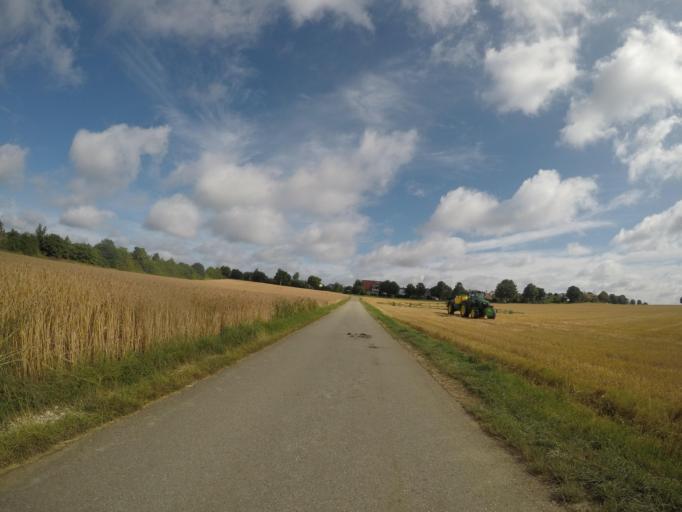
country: DE
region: Baden-Wuerttemberg
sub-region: Tuebingen Region
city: Laichingen
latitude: 48.4370
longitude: 9.6584
